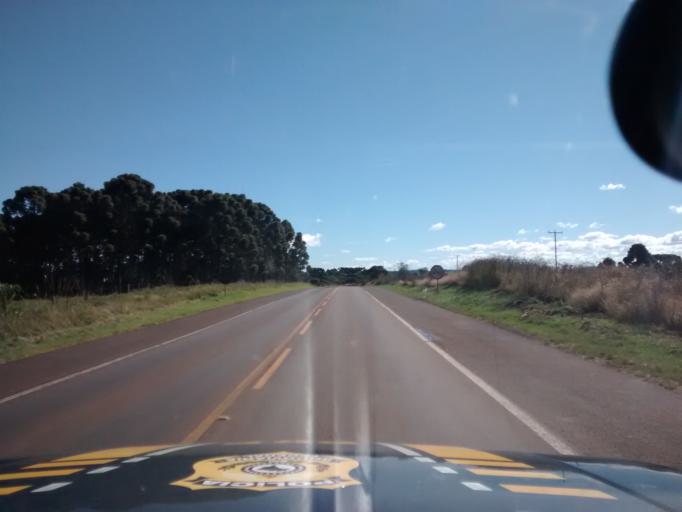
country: BR
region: Rio Grande do Sul
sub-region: Vacaria
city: Vacaria
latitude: -28.3553
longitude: -51.1125
